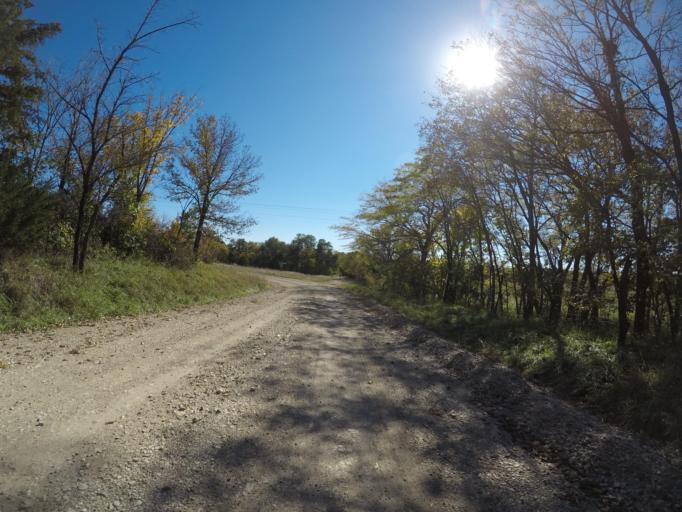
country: US
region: Kansas
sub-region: Wabaunsee County
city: Alma
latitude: 38.9824
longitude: -96.4555
